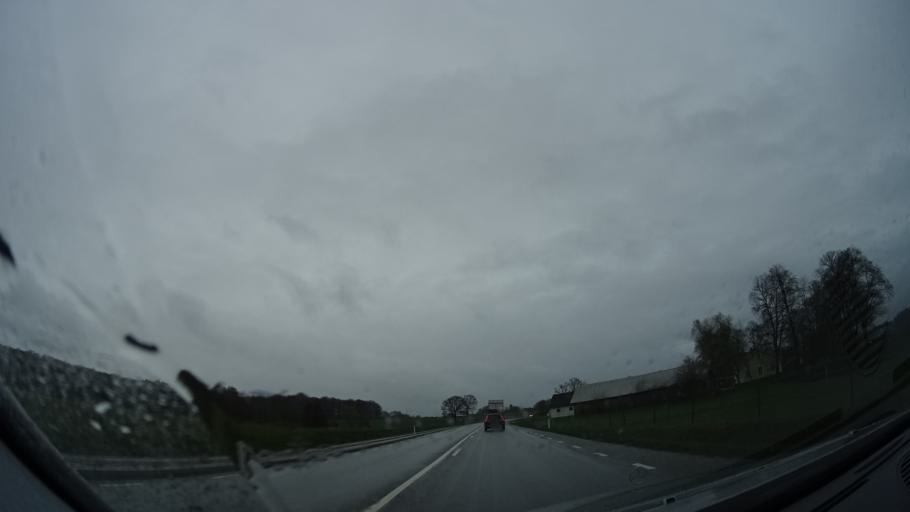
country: SE
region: Skane
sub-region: Hoors Kommun
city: Loberod
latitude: 55.8155
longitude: 13.4785
